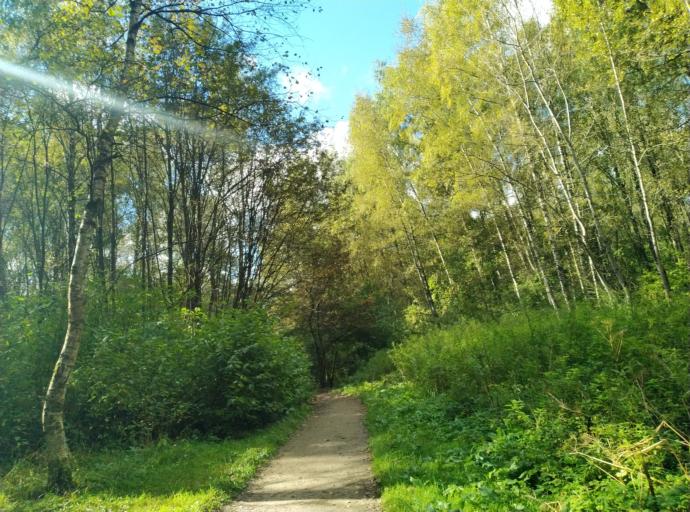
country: RU
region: Moscow
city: Khimki
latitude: 55.8659
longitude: 37.4193
